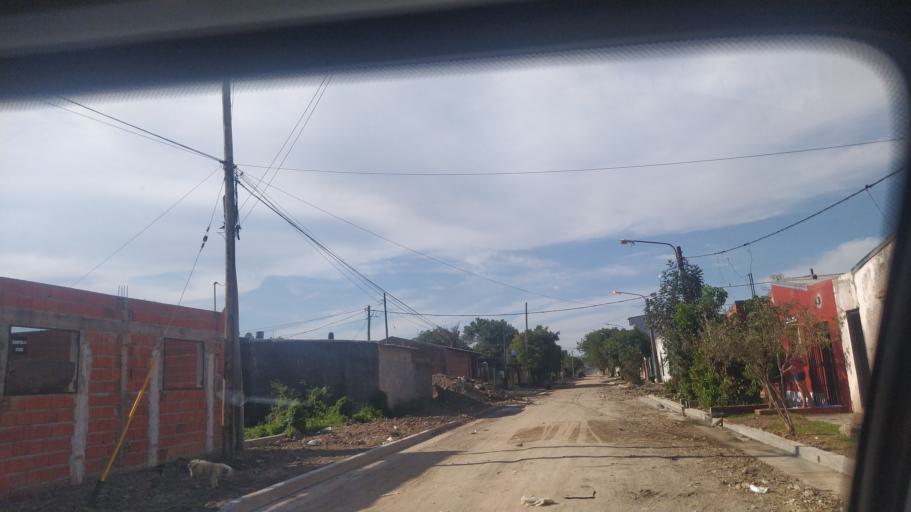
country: AR
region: Corrientes
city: Corrientes
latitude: -27.4904
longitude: -58.8119
